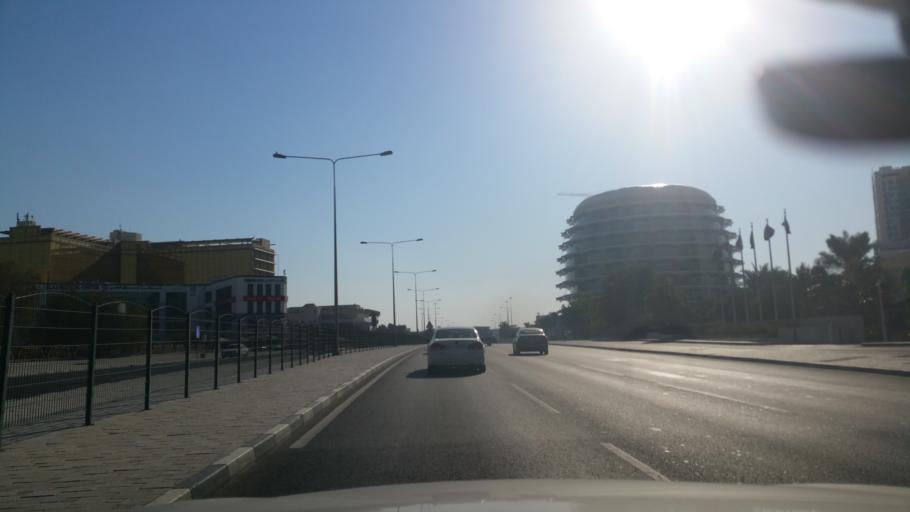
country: QA
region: Baladiyat ad Dawhah
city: Doha
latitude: 25.2755
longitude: 51.5146
